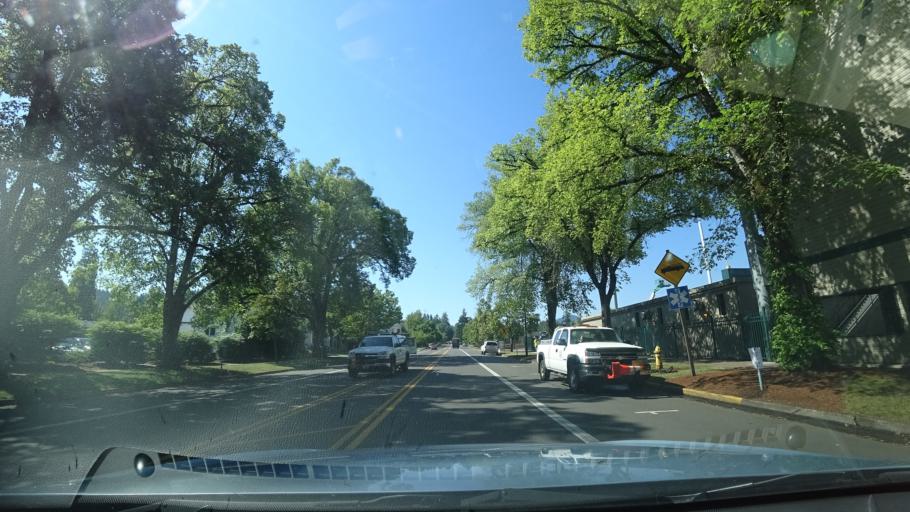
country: US
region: Oregon
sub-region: Lane County
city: Eugene
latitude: 44.0423
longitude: -123.0697
